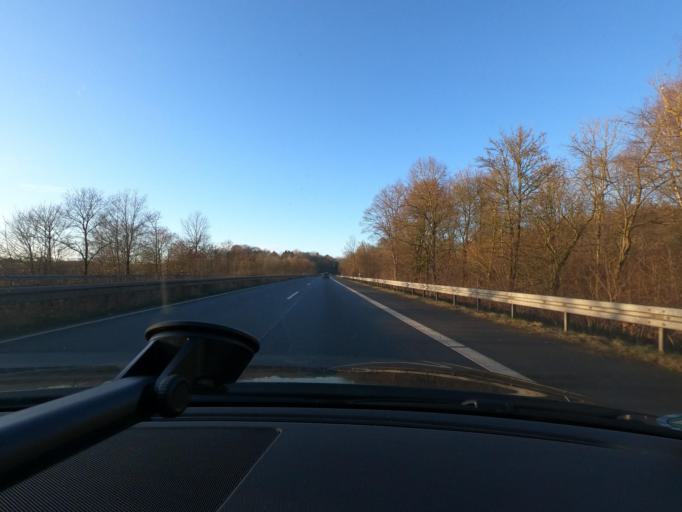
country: DE
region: Lower Saxony
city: Hoerden
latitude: 51.6913
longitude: 10.2961
